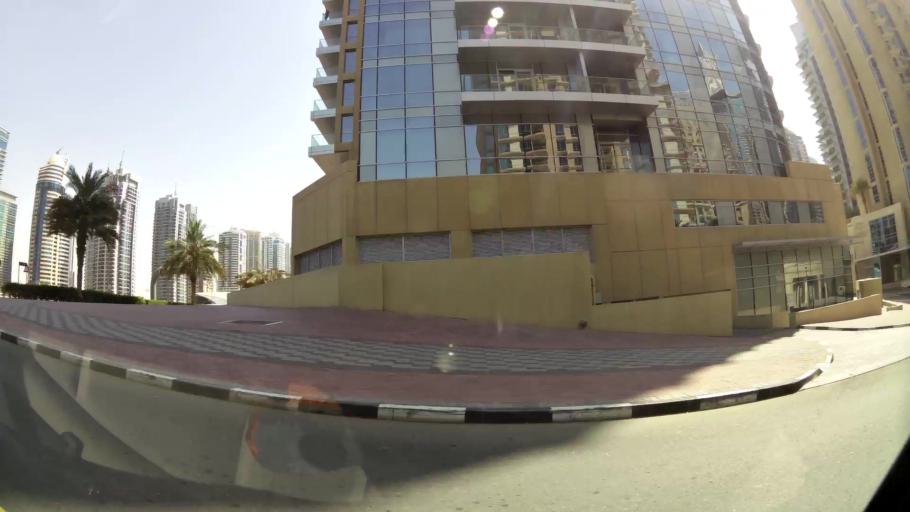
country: AE
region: Dubai
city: Dubai
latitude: 25.0829
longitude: 55.1483
